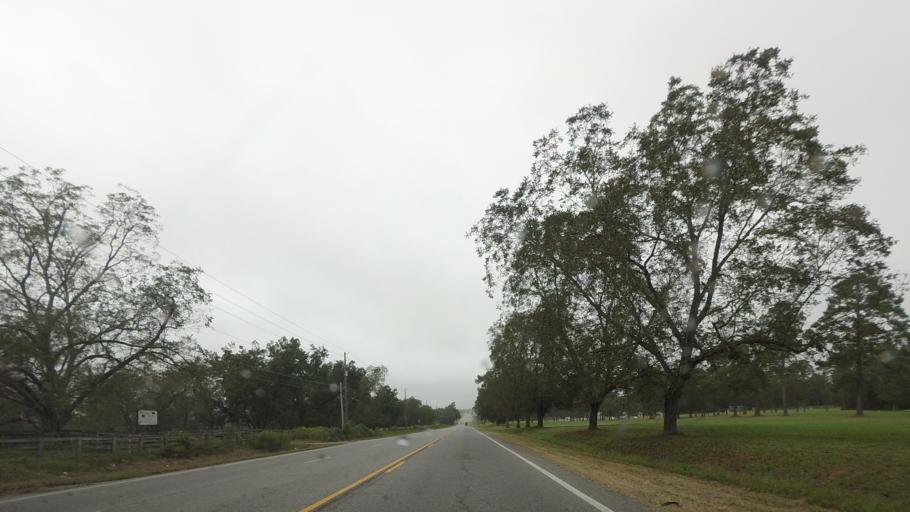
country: US
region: Georgia
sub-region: Ben Hill County
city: Fitzgerald
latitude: 31.6856
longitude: -83.2399
